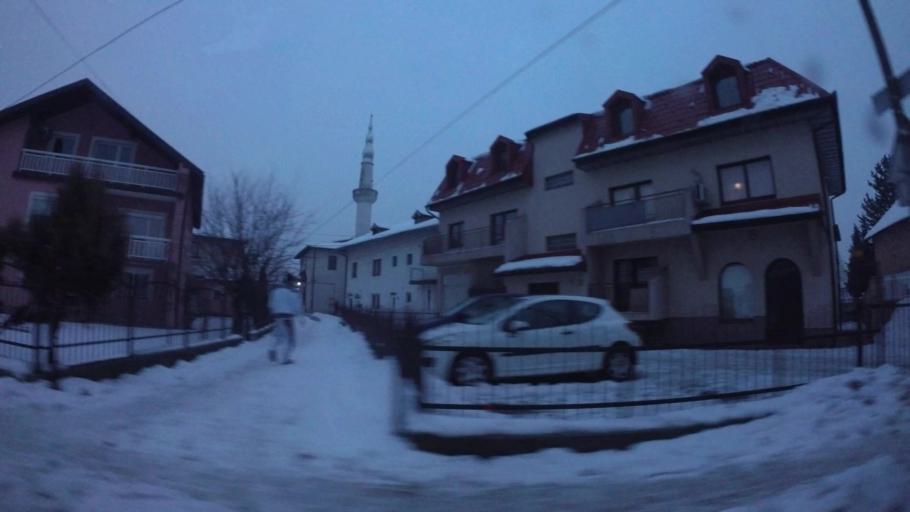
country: BA
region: Federation of Bosnia and Herzegovina
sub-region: Kanton Sarajevo
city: Sarajevo
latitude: 43.8376
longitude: 18.2987
